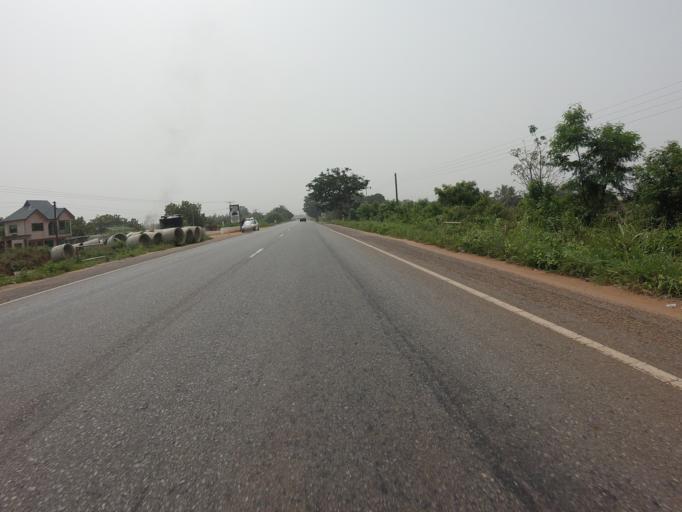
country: GH
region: Volta
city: Anloga
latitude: 5.9068
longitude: 0.5225
